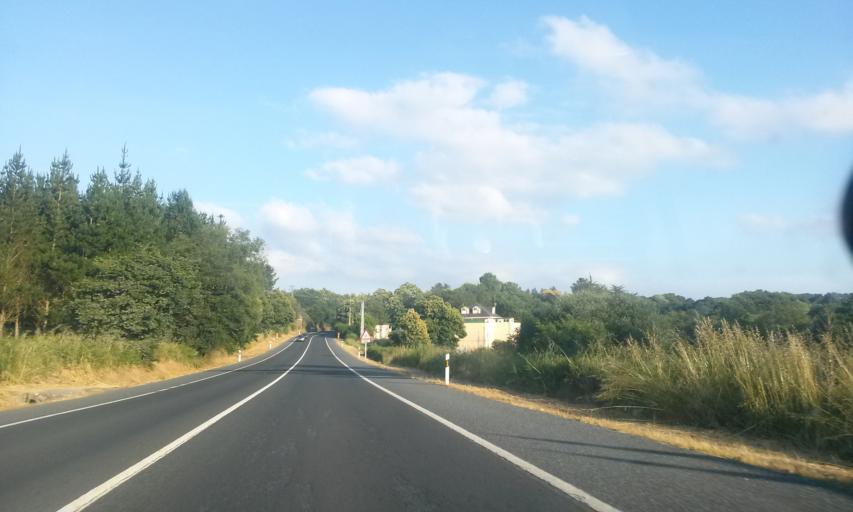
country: ES
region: Galicia
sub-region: Provincia de Lugo
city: Outeiro de Rei
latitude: 43.0722
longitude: -7.6030
